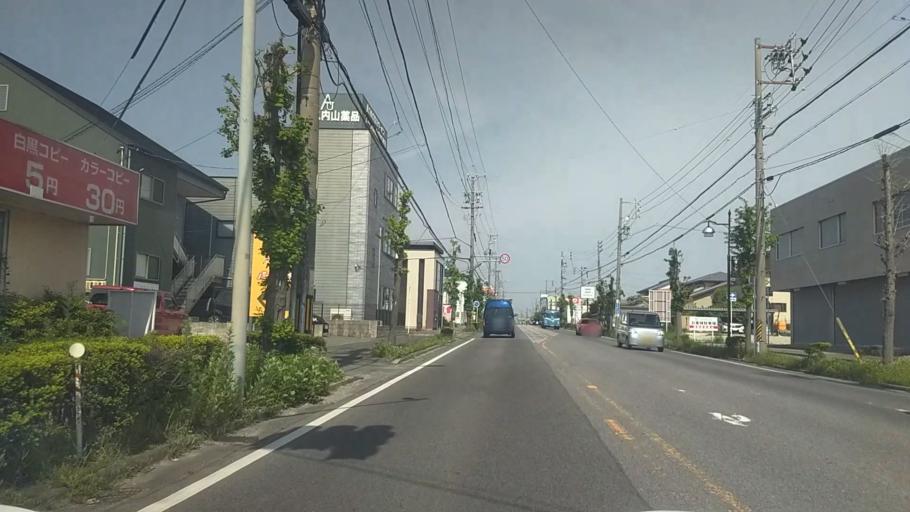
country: JP
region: Aichi
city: Anjo
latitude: 34.9508
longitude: 137.0865
